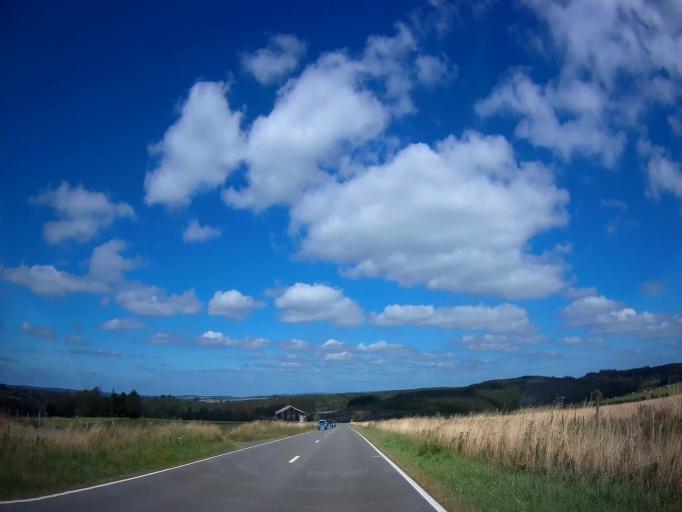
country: BE
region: Wallonia
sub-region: Province du Luxembourg
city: Bastogne
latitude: 50.0241
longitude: 5.7046
